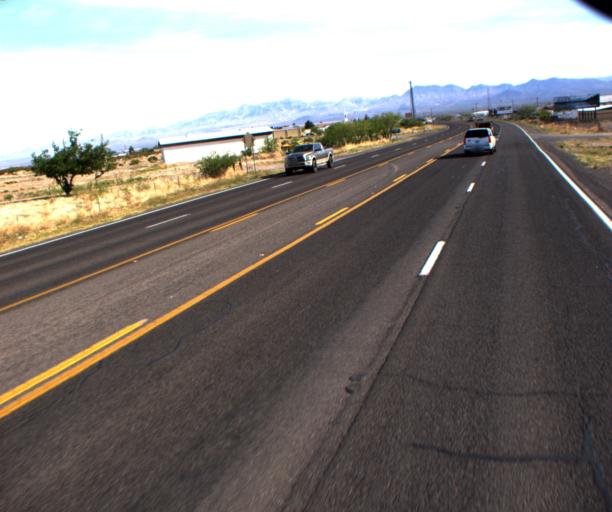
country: US
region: Arizona
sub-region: Graham County
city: Cactus Flat
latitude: 32.7882
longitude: -109.7098
